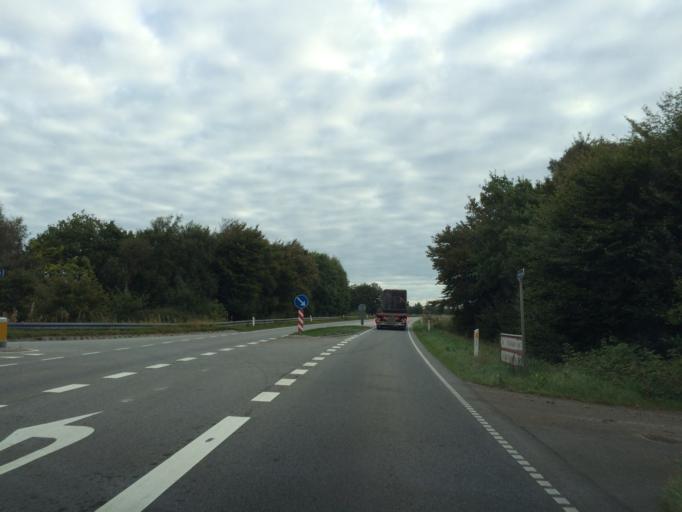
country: DK
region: Central Jutland
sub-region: Ringkobing-Skjern Kommune
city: Skjern
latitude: 55.9659
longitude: 8.5523
